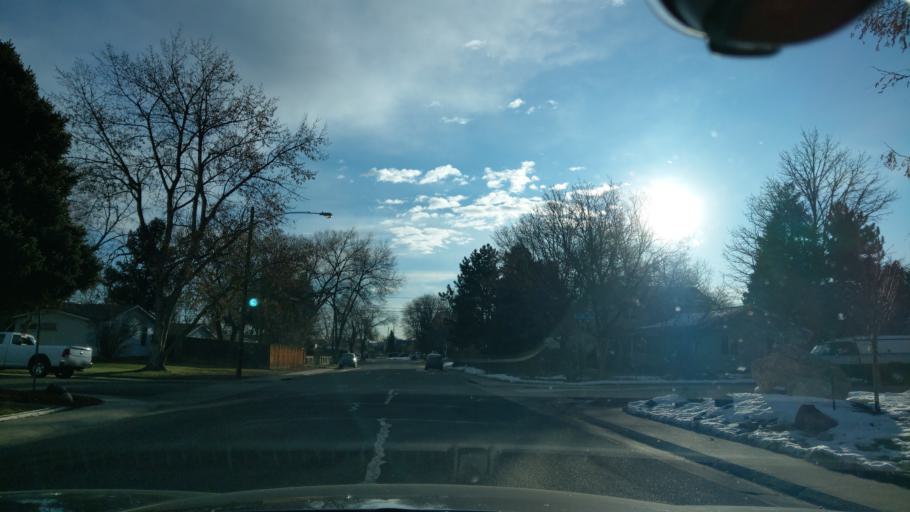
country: US
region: Colorado
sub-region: Jefferson County
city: Lakewood
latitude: 39.7307
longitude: -105.1127
